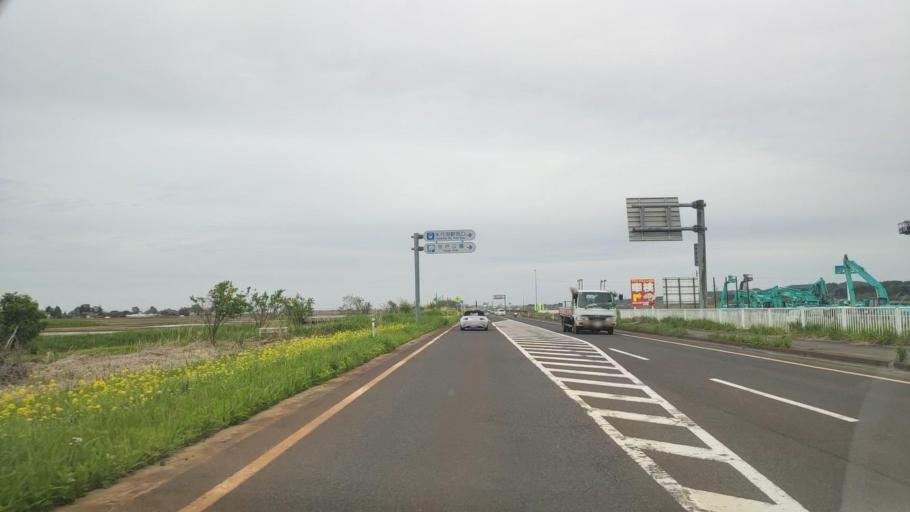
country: JP
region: Niigata
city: Niitsu-honcho
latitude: 37.7515
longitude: 139.0879
